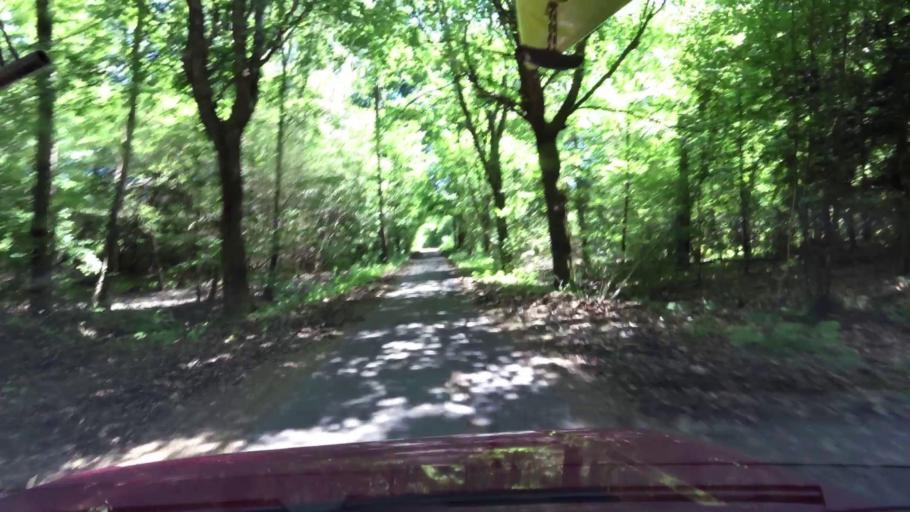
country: PL
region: West Pomeranian Voivodeship
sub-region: Powiat koszalinski
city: Polanow
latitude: 54.0354
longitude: 16.7903
